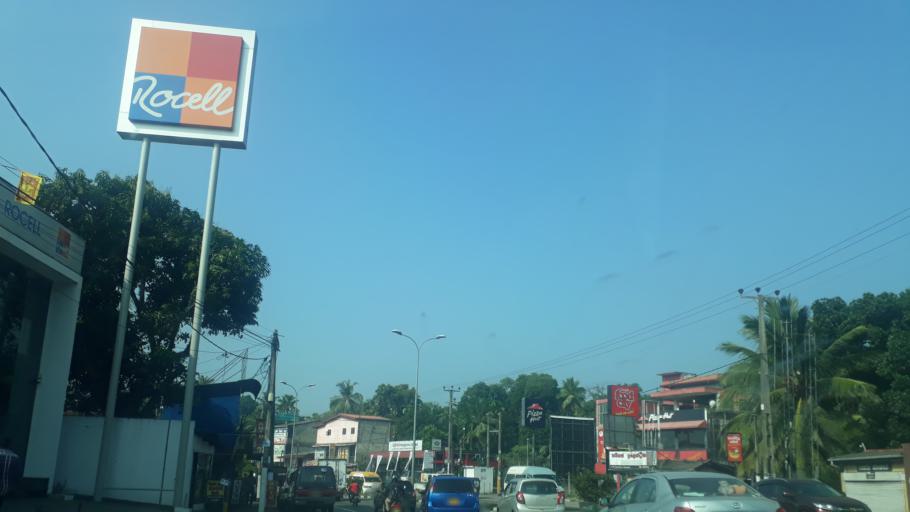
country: LK
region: Western
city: Kelaniya
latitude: 7.0006
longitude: 79.9490
